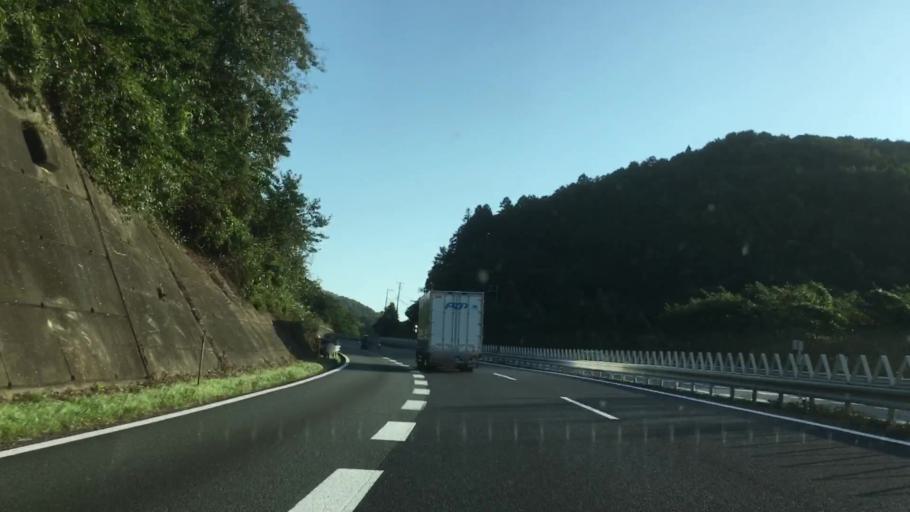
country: JP
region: Yamaguchi
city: Onoda
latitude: 34.1507
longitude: 131.2341
